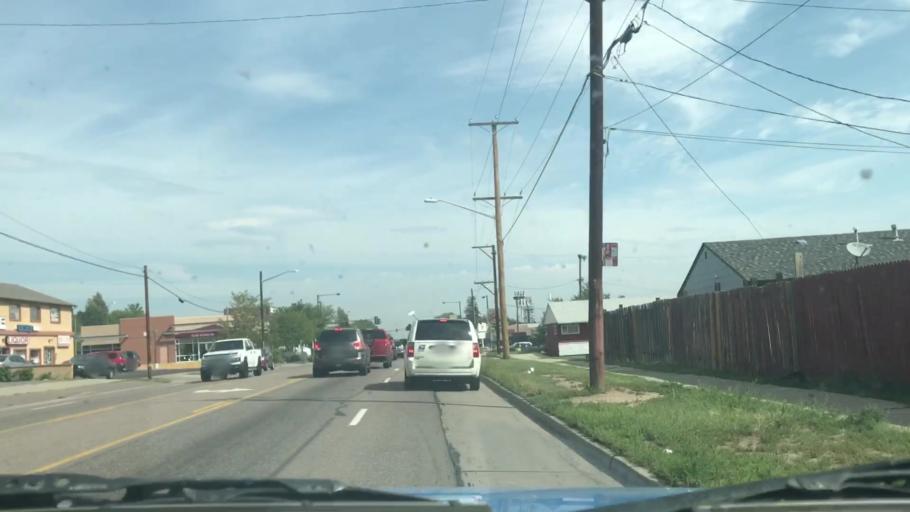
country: US
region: Colorado
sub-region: Jefferson County
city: Lakewood
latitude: 39.7098
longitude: -105.0532
